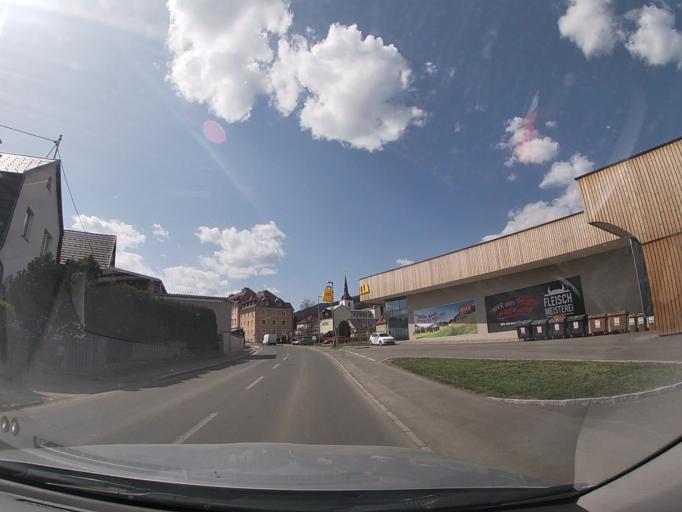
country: AT
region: Styria
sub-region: Politischer Bezirk Murtal
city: Fohnsdorf
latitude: 47.2077
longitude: 14.6821
